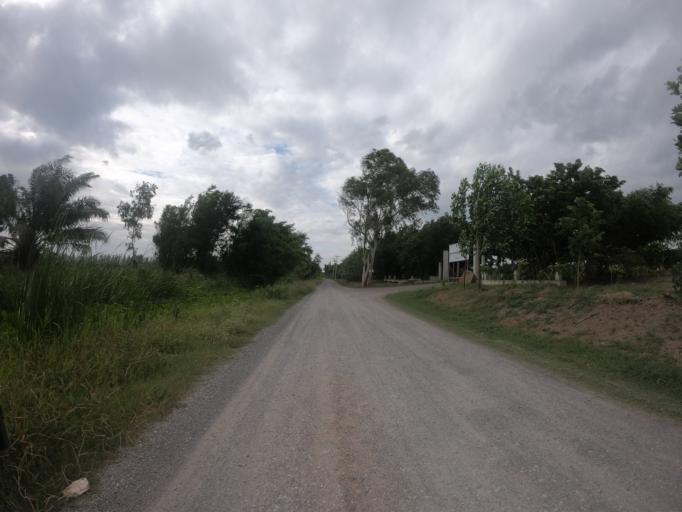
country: TH
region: Pathum Thani
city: Nong Suea
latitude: 14.0734
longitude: 100.8353
